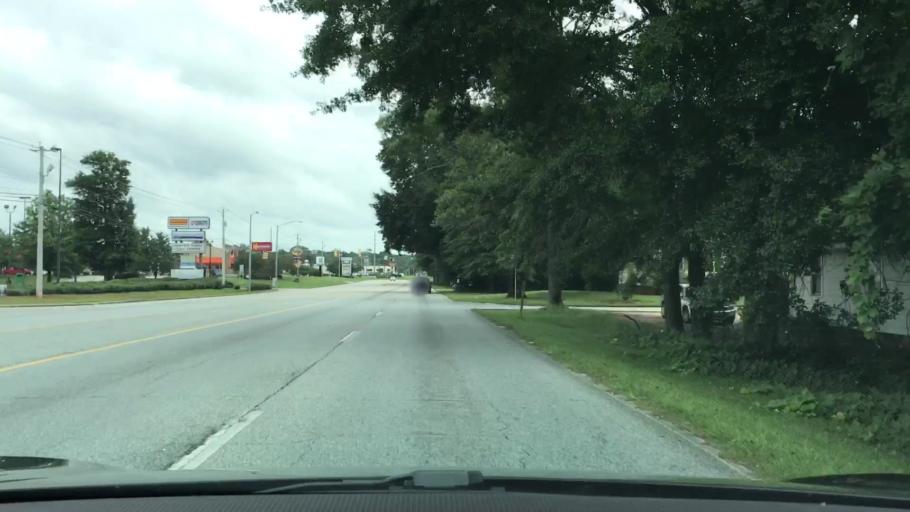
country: US
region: Alabama
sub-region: Lee County
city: Opelika
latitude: 32.6369
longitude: -85.4157
